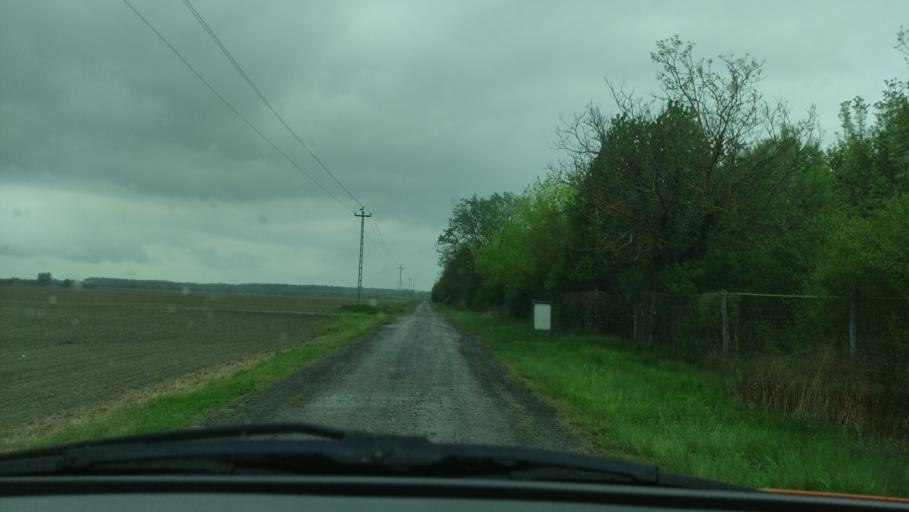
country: HR
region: Osjecko-Baranjska
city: Batina
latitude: 45.8995
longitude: 18.7799
